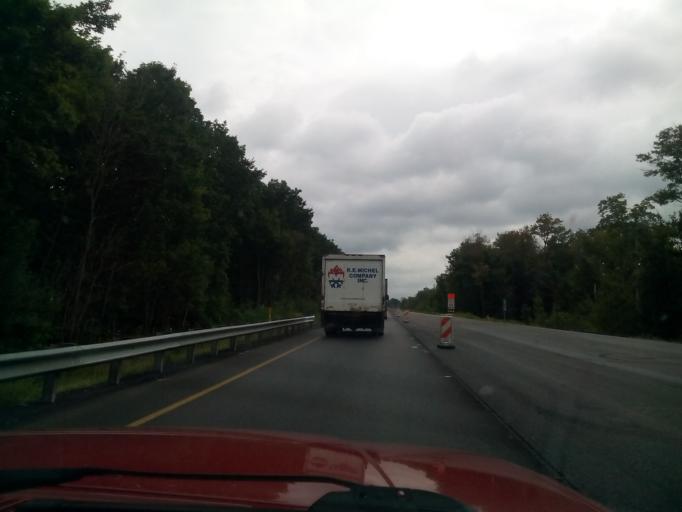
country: US
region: Pennsylvania
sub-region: Jefferson County
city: Reynoldsville
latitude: 41.1516
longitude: -78.8856
